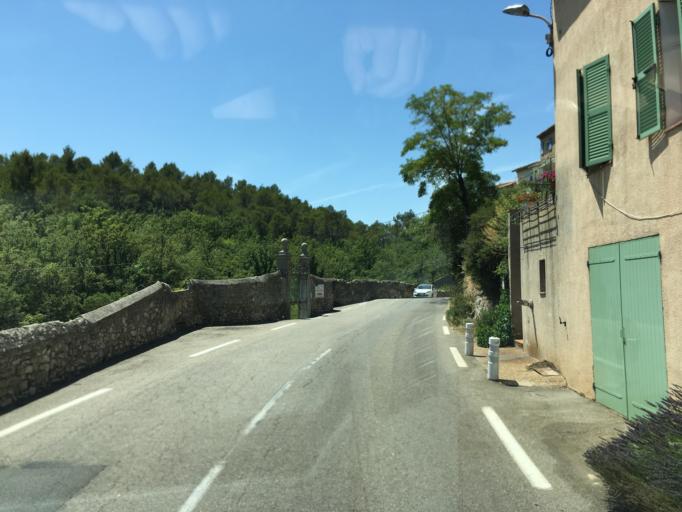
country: FR
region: Provence-Alpes-Cote d'Azur
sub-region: Departement du Var
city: Saint-Maximin-la-Sainte-Baume
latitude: 43.4824
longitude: 5.8307
